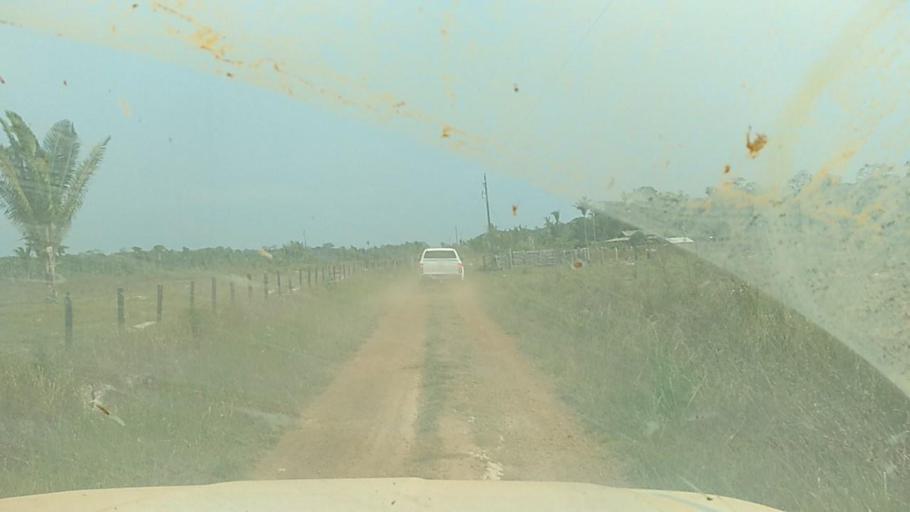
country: BR
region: Rondonia
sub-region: Porto Velho
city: Porto Velho
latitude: -8.9737
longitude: -64.3839
